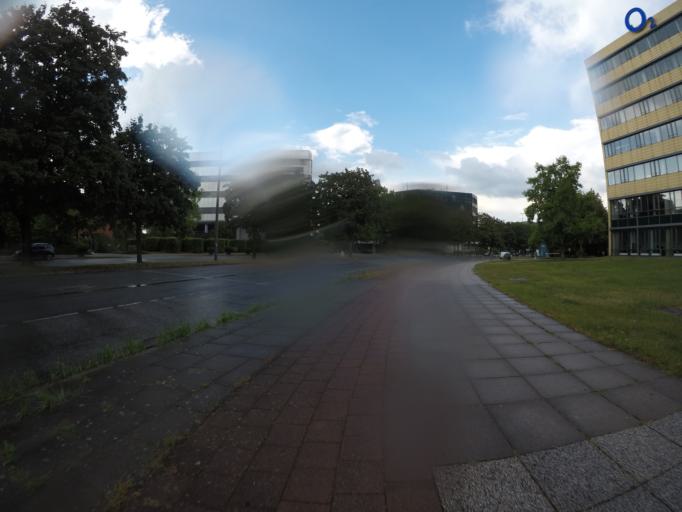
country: DE
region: Hamburg
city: Alsterdorf
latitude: 53.6060
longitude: 10.0184
